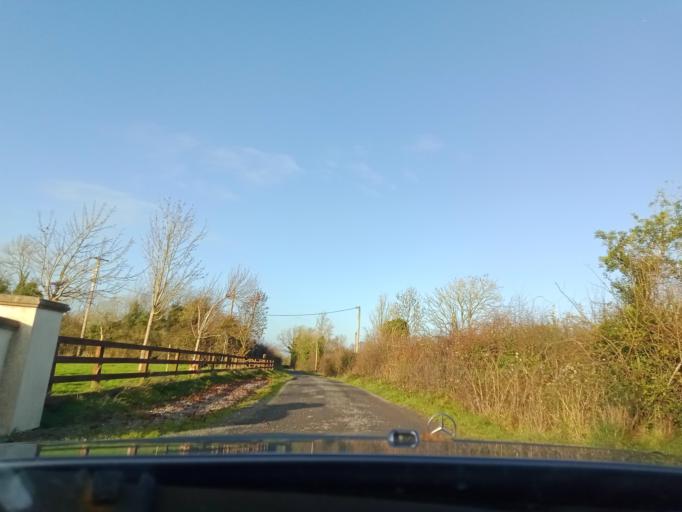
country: IE
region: Leinster
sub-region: Kilkenny
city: Callan
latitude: 52.5198
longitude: -7.4004
